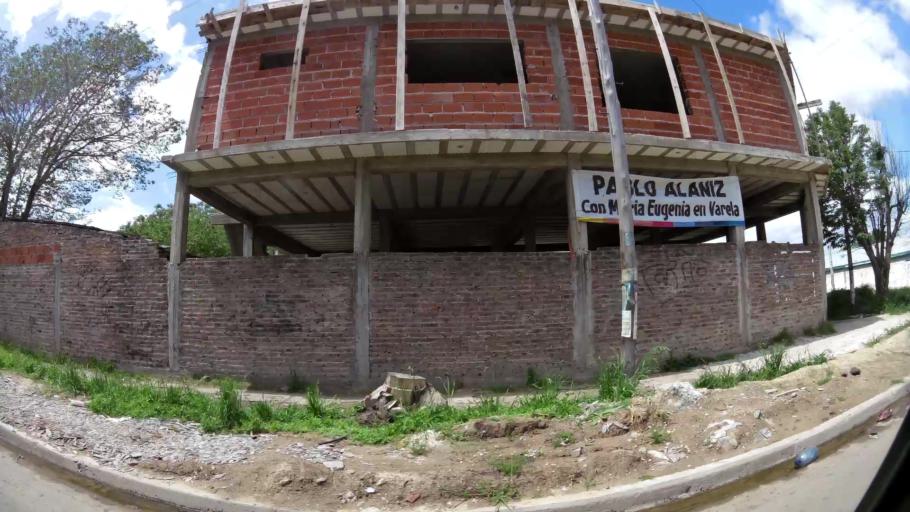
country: AR
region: Buenos Aires
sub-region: Partido de Quilmes
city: Quilmes
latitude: -34.8397
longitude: -58.2320
